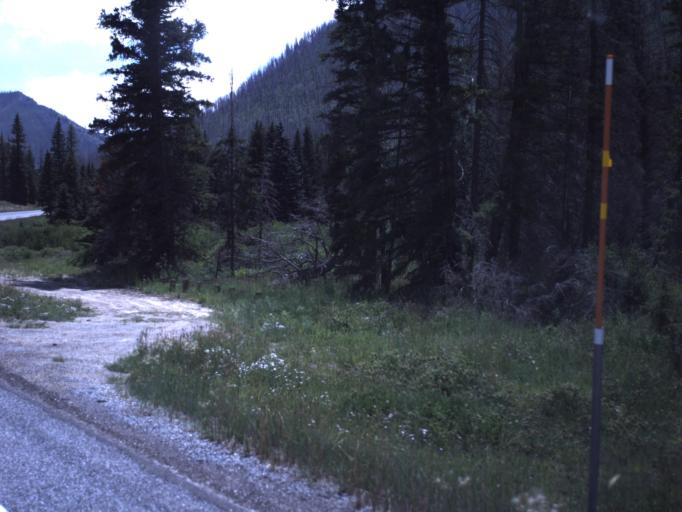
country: US
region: Utah
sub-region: Emery County
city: Huntington
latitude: 39.5413
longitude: -111.1612
